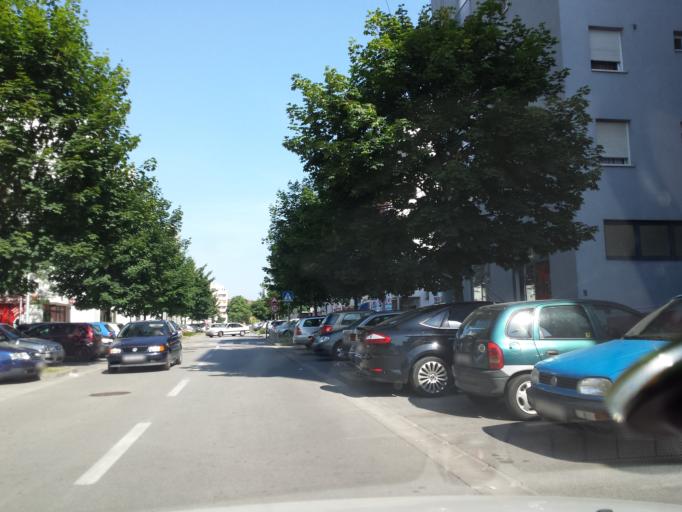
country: HR
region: Grad Zagreb
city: Jankomir
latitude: 45.7976
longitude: 15.9060
